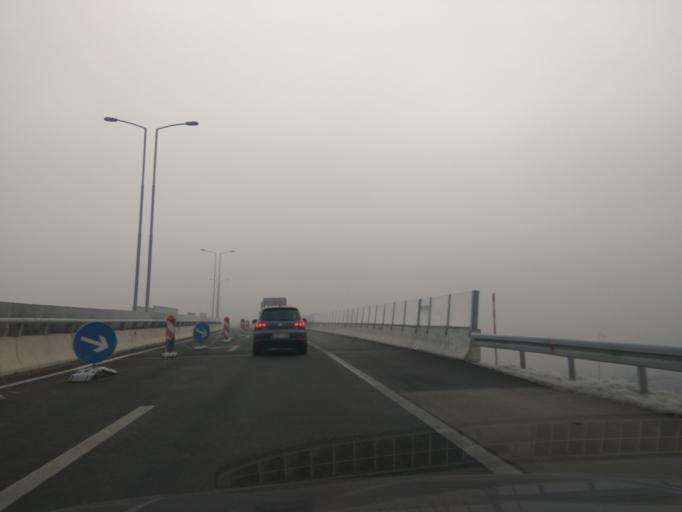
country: BA
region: Federation of Bosnia and Herzegovina
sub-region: Kanton Sarajevo
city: Sarajevo
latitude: 43.8516
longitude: 18.3184
